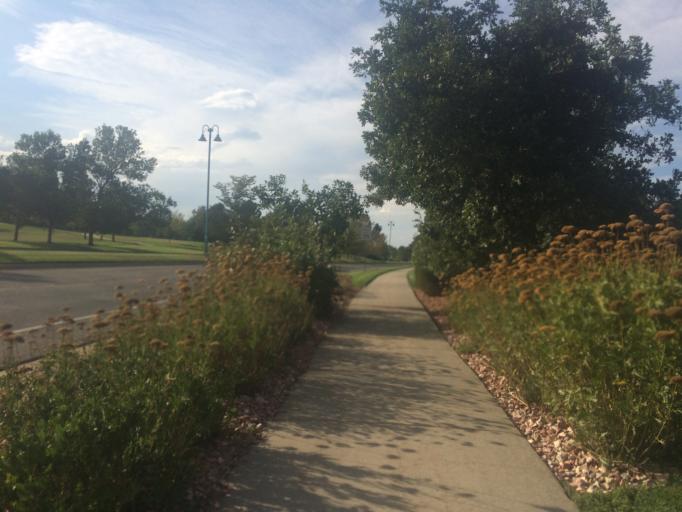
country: US
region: Colorado
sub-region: Boulder County
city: Superior
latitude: 39.9410
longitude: -105.1568
